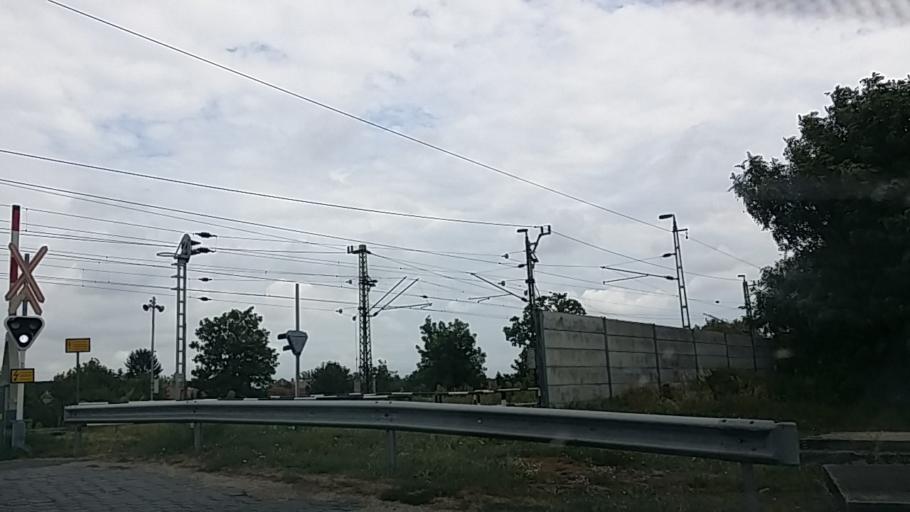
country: HU
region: Komarom-Esztergom
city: Acs
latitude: 47.7172
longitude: 18.0112
